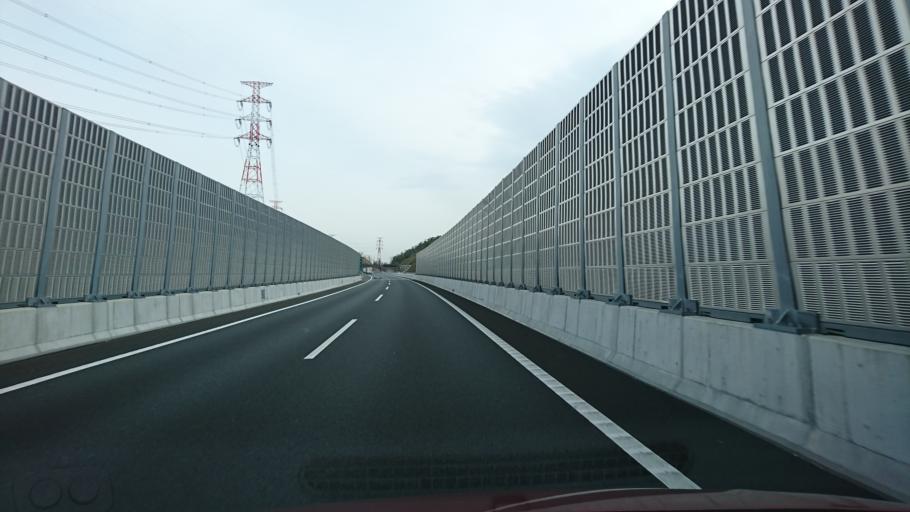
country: JP
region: Hyogo
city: Sandacho
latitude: 34.8575
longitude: 135.2505
